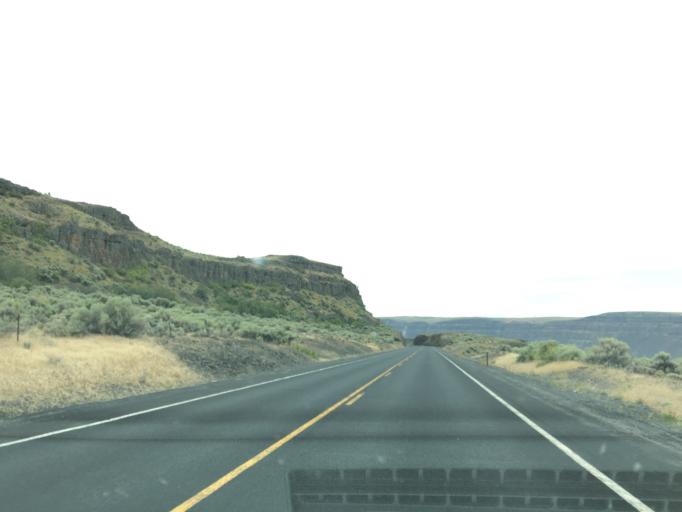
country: US
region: Washington
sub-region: Okanogan County
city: Coulee Dam
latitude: 47.7361
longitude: -119.2387
